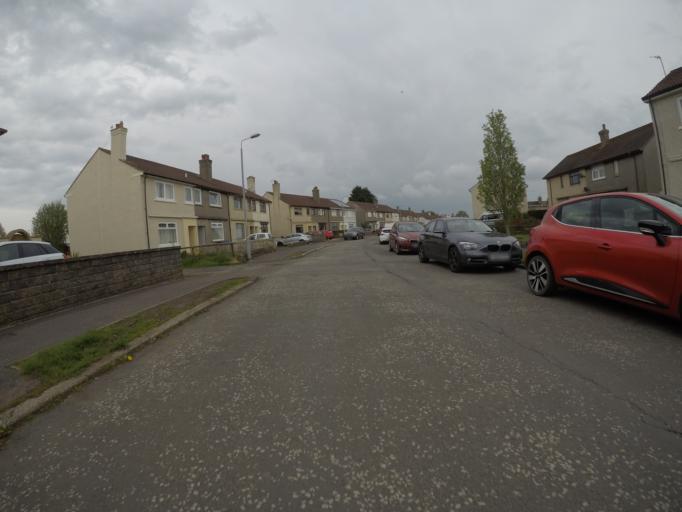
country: GB
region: Scotland
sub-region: East Ayrshire
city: Kilmaurs
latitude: 55.6417
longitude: -4.5311
